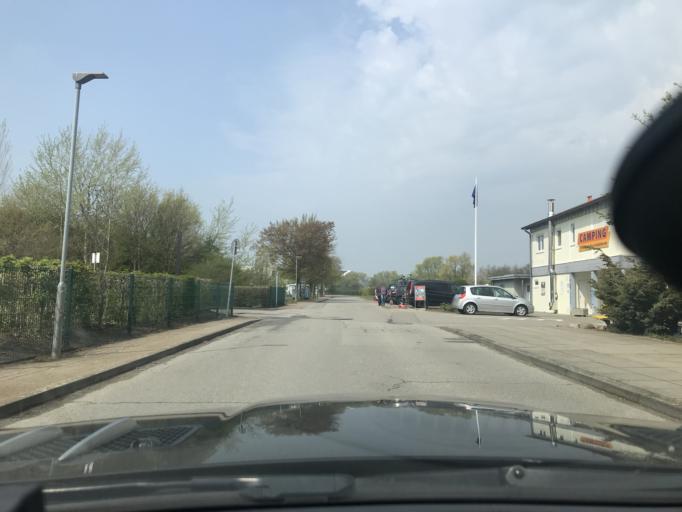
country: DE
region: Schleswig-Holstein
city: Grossenbrode
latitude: 54.3601
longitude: 11.0876
